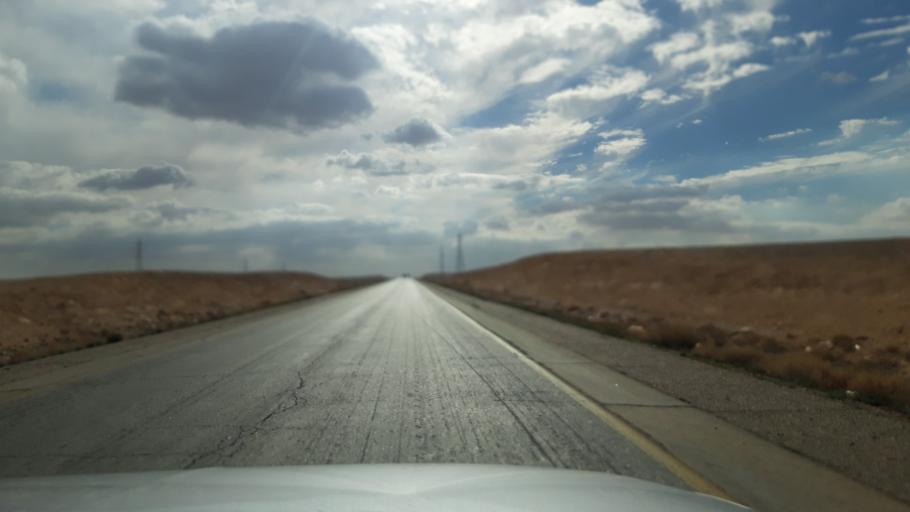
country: JO
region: Amman
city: Al Azraq ash Shamali
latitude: 31.7407
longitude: 36.5290
